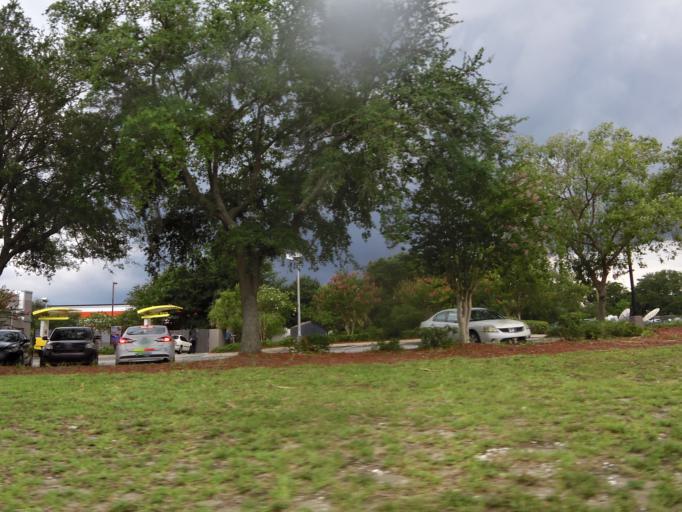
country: US
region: Florida
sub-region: Duval County
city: Jacksonville
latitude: 30.3232
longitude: -81.5435
